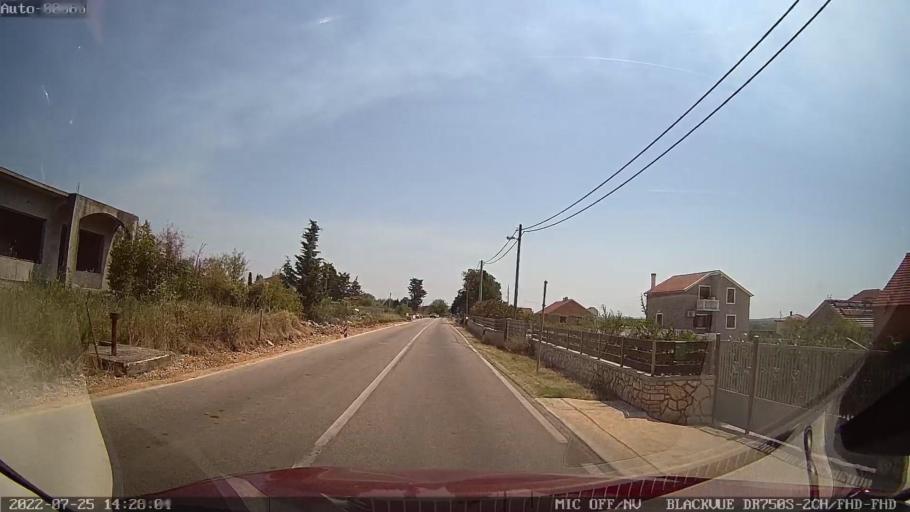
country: HR
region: Zadarska
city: Policnik
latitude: 44.1288
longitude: 15.3476
